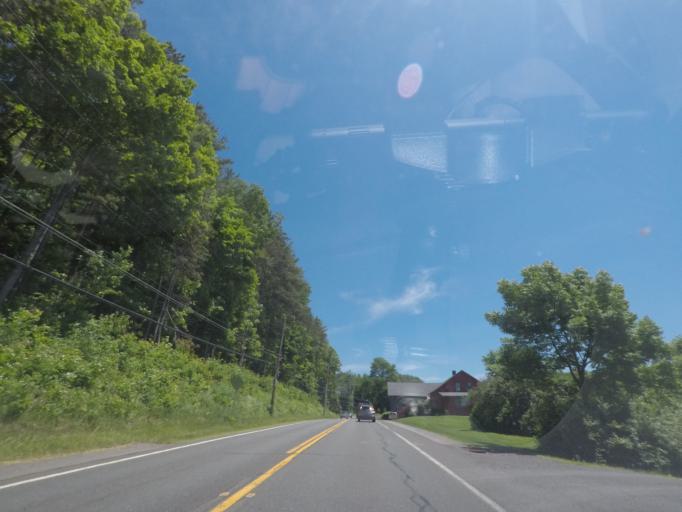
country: US
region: Massachusetts
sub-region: Berkshire County
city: Lee
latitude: 42.2960
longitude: -73.1787
